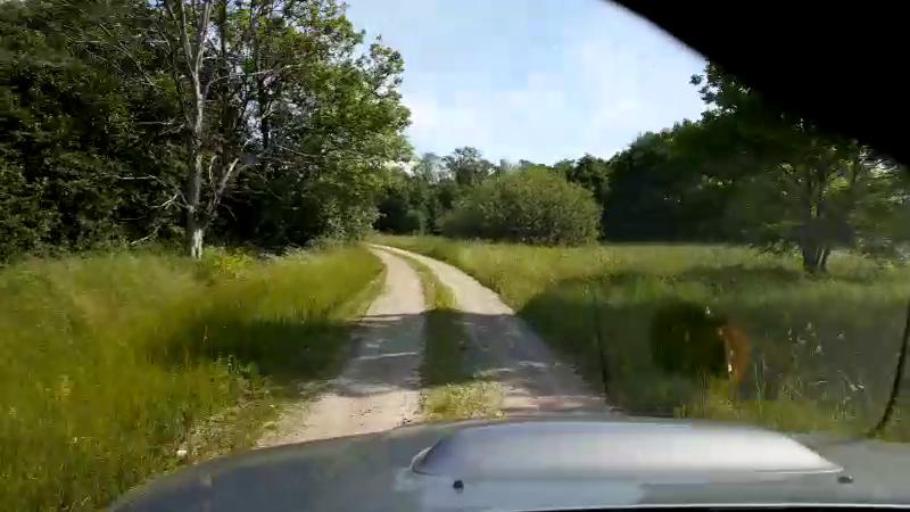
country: EE
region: Paernumaa
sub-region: Sauga vald
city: Sauga
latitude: 58.4961
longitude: 24.5391
